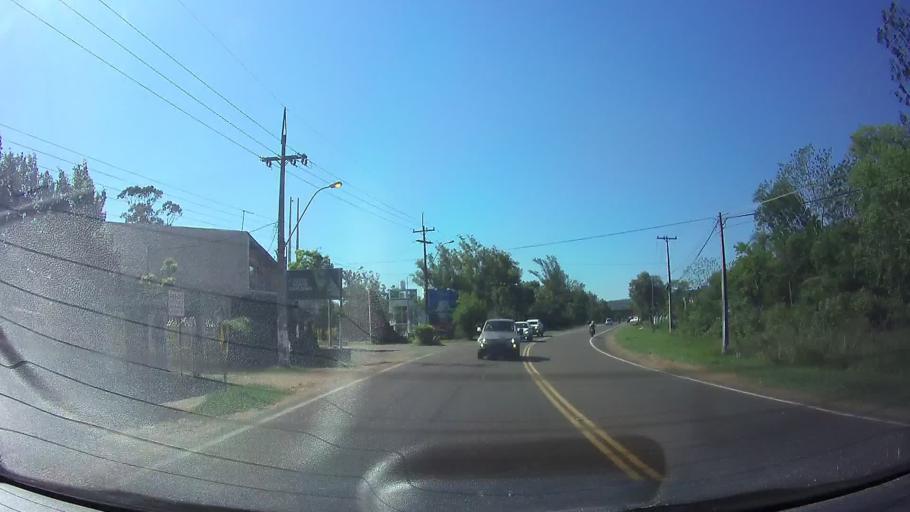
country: PY
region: Cordillera
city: San Bernardino
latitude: -25.3422
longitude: -57.2741
